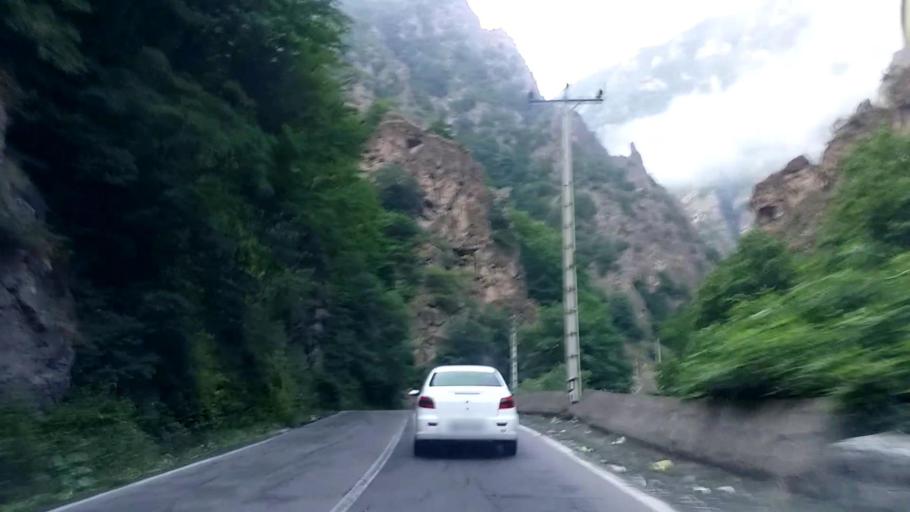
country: IR
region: Mazandaran
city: Chalus
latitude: 36.2781
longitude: 51.2443
